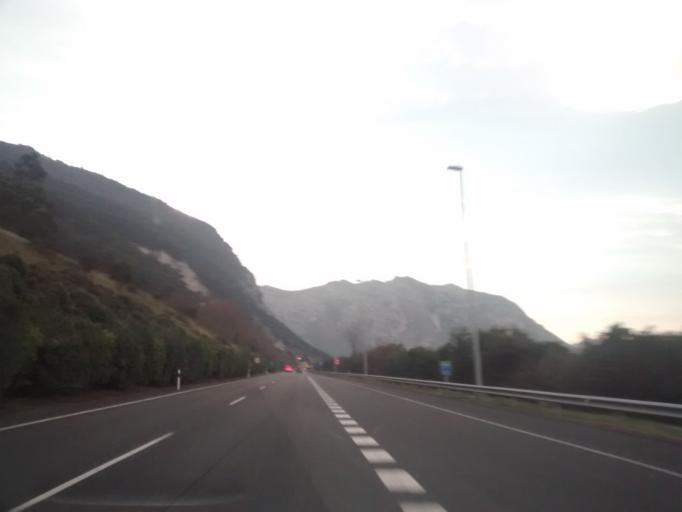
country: ES
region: Cantabria
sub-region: Provincia de Cantabria
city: Liendo
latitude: 43.4025
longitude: -3.2999
